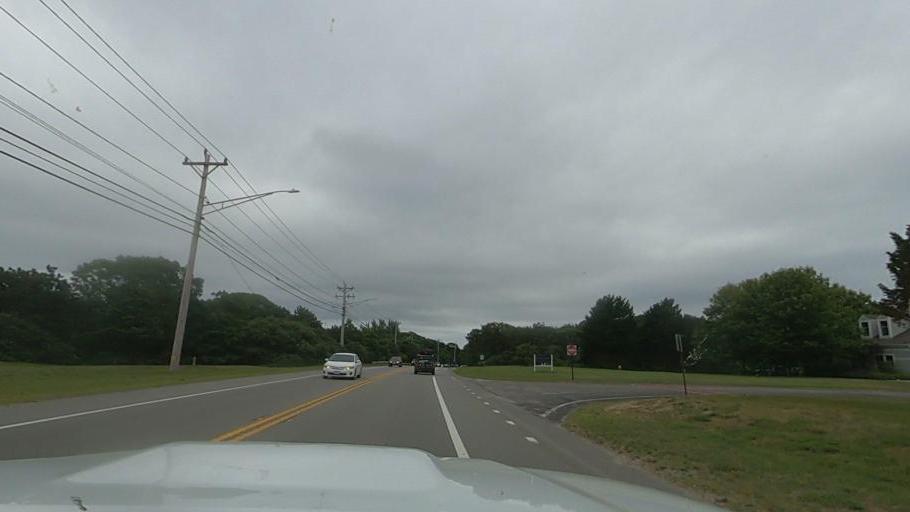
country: US
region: Massachusetts
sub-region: Barnstable County
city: Truro
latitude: 42.0228
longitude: -70.0737
